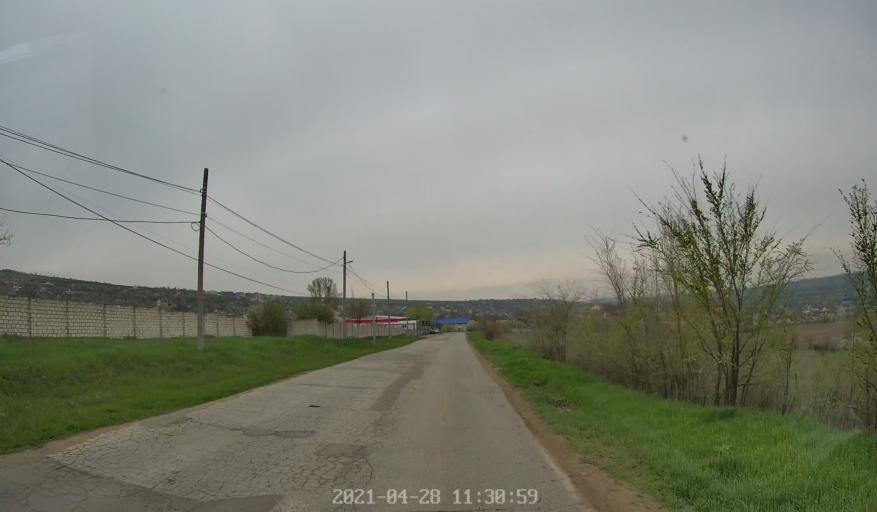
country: MD
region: Chisinau
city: Singera
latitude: 46.9720
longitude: 28.9379
